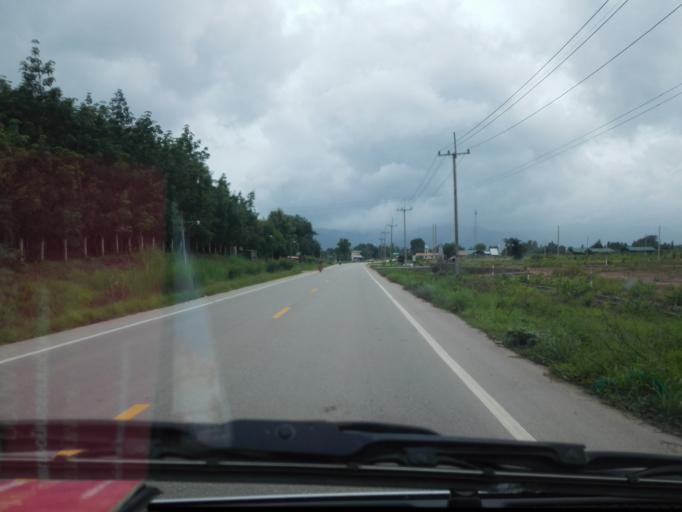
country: TH
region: Tak
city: Mae Sot
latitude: 16.6956
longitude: 98.4174
